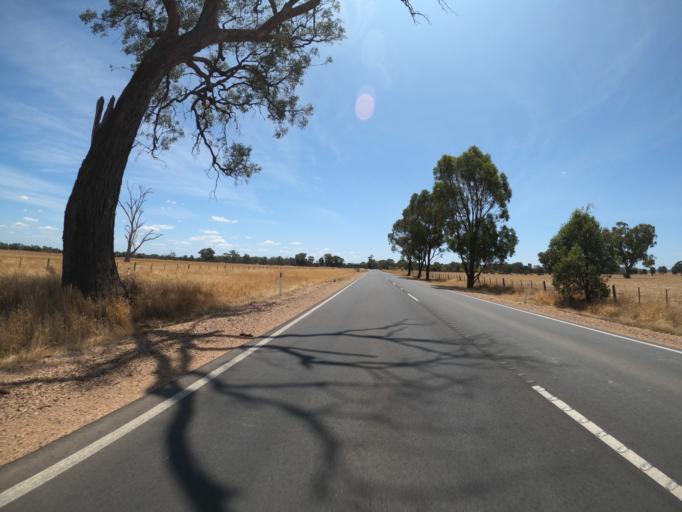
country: AU
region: Victoria
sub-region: Benalla
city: Benalla
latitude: -36.5007
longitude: 146.0221
